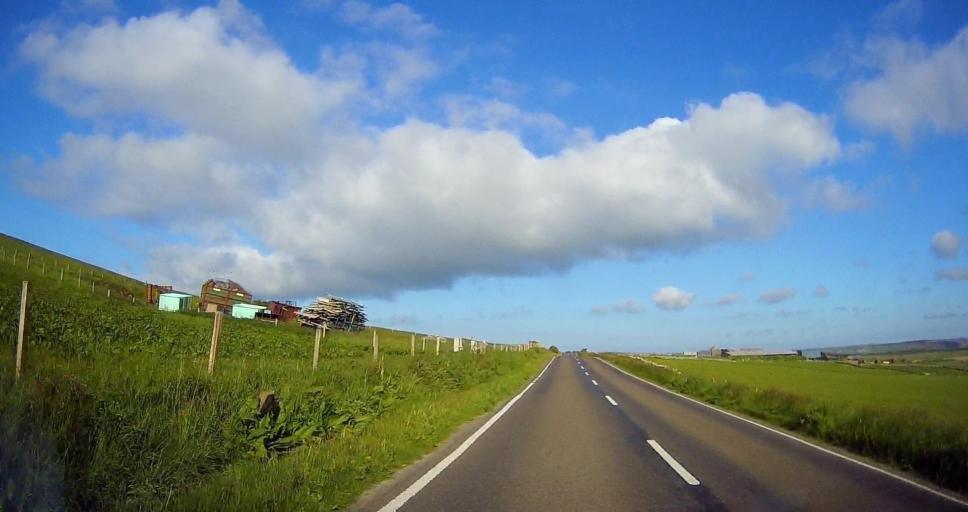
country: GB
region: Scotland
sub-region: Orkney Islands
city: Orkney
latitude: 58.9800
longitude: -3.0300
